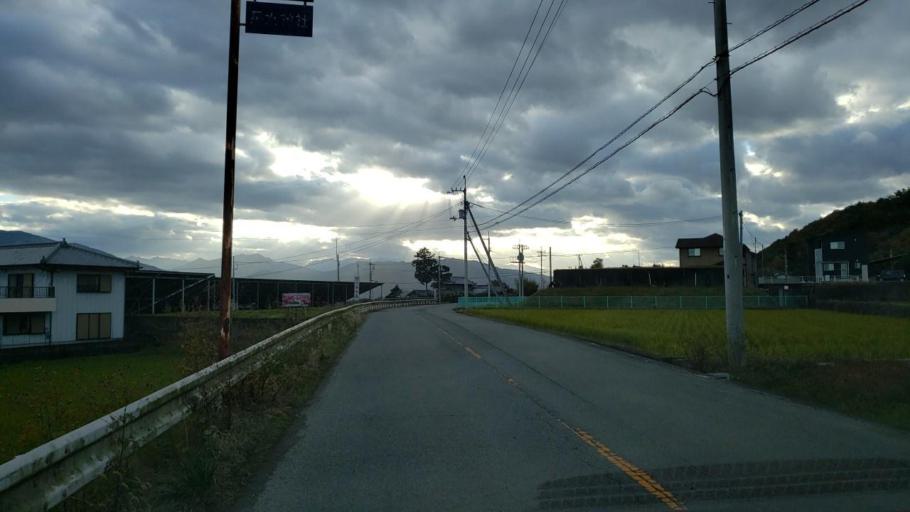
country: JP
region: Tokushima
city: Wakimachi
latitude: 34.0930
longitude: 134.2125
